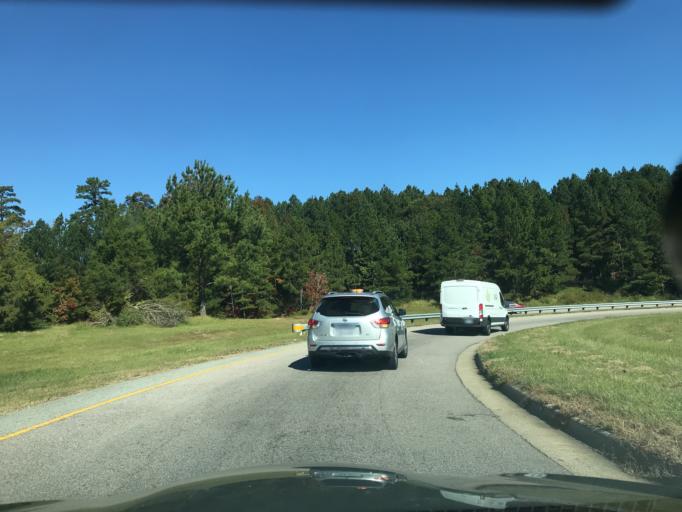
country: US
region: North Carolina
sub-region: Durham County
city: Durham
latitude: 36.0178
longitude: -78.9526
